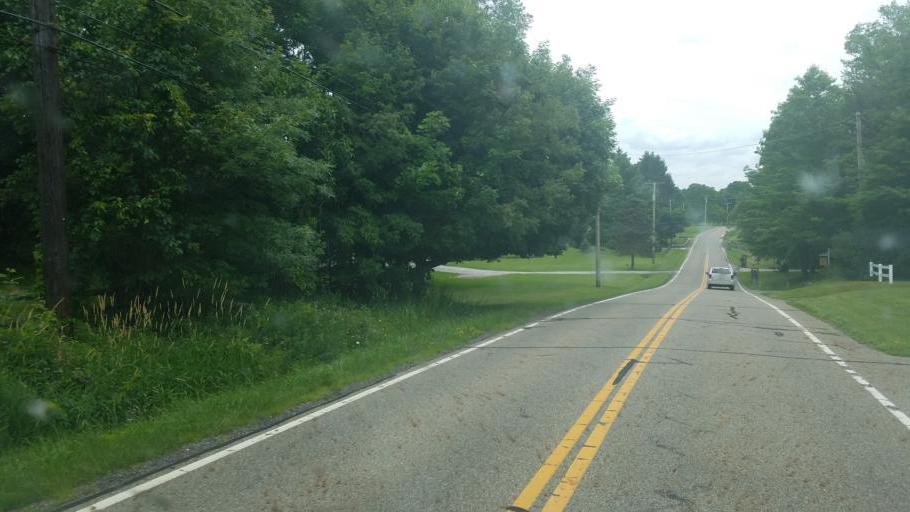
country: US
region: Ohio
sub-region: Geauga County
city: Burton
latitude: 41.4975
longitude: -81.1794
